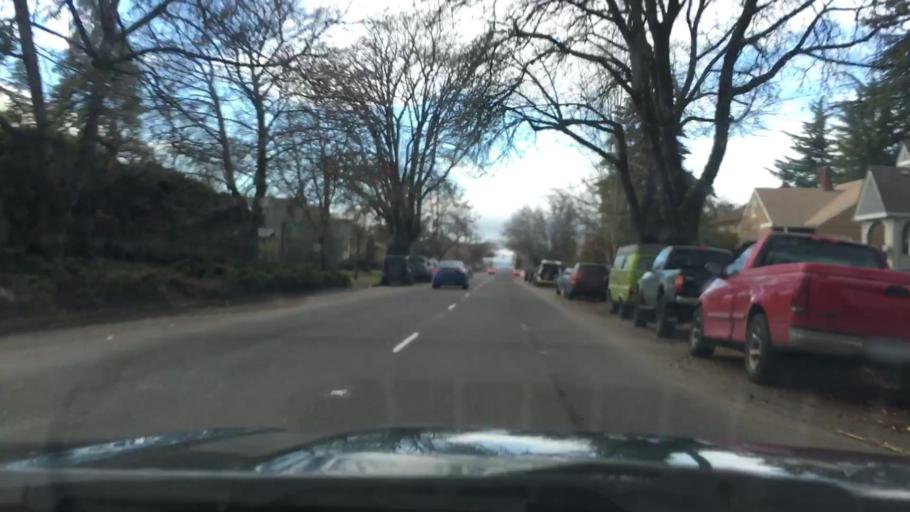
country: US
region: Oregon
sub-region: Lane County
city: Eugene
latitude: 44.0478
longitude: -123.1143
